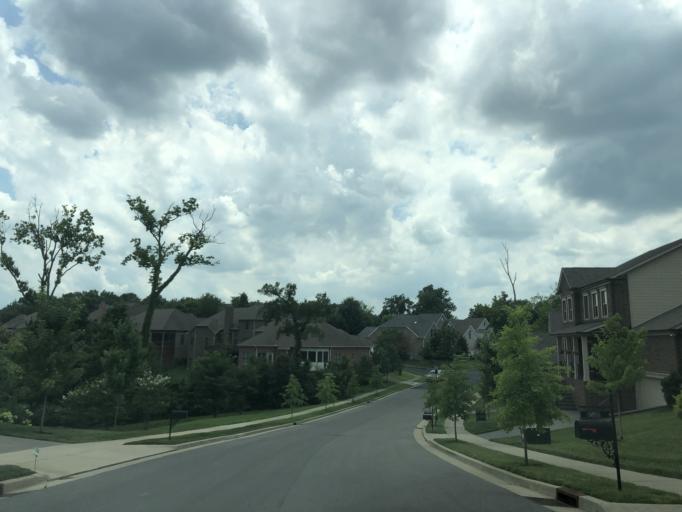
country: US
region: Tennessee
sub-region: Williamson County
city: Brentwood Estates
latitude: 36.0264
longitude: -86.7259
